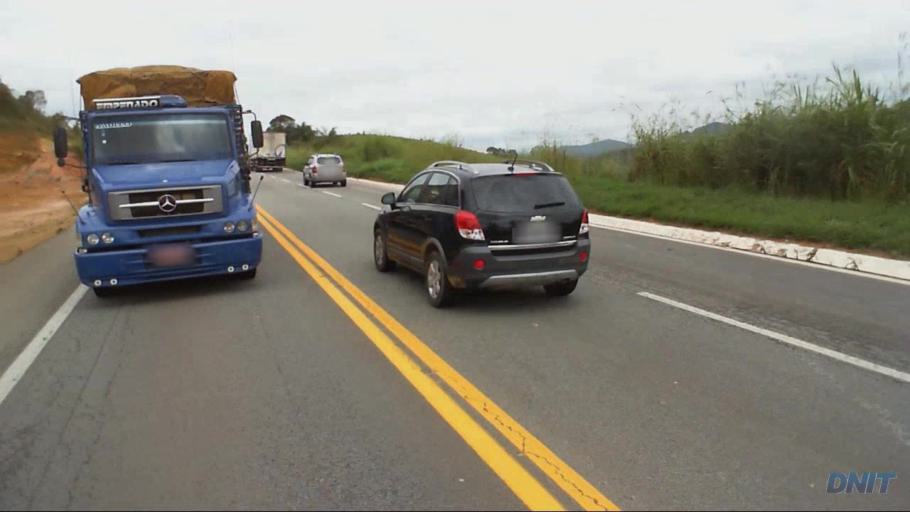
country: BR
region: Minas Gerais
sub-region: Caete
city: Caete
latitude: -19.7314
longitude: -43.5599
